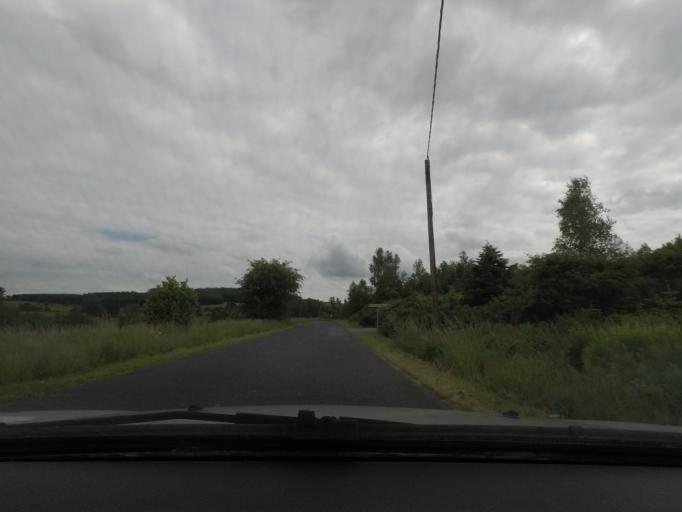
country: BE
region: Wallonia
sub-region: Province du Luxembourg
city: Leglise
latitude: 49.8105
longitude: 5.5411
